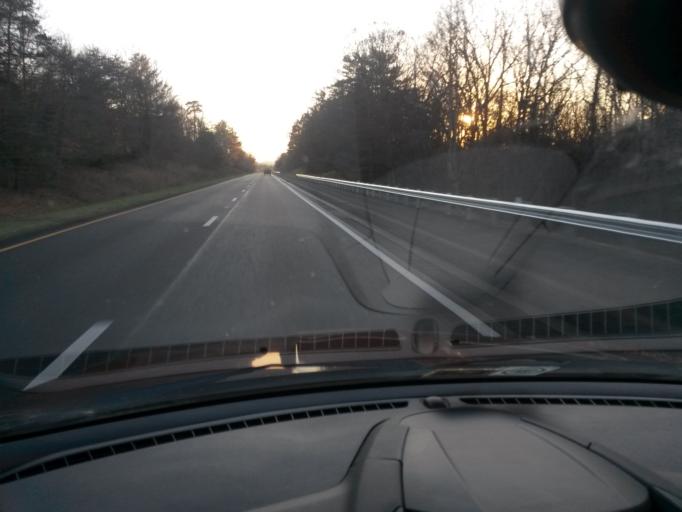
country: US
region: Virginia
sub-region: Alleghany County
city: Clifton Forge
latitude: 37.8225
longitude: -79.6632
